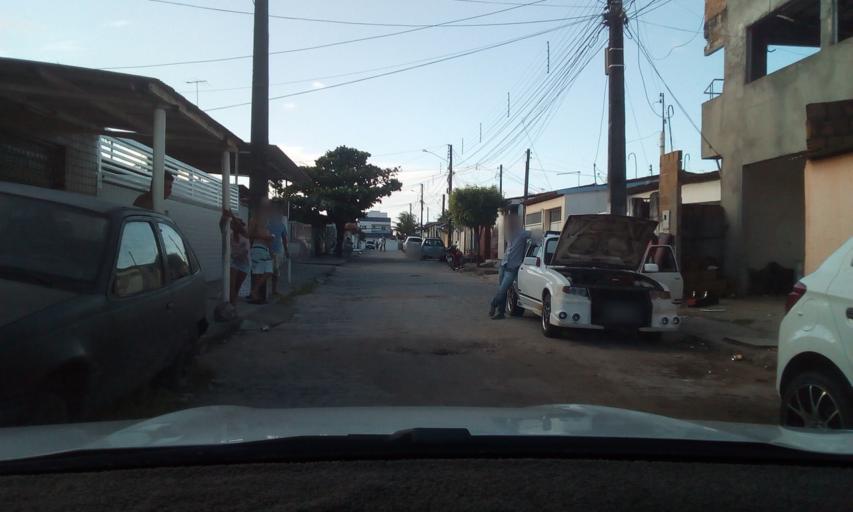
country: BR
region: Paraiba
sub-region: Joao Pessoa
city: Joao Pessoa
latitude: -7.1852
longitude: -34.8377
